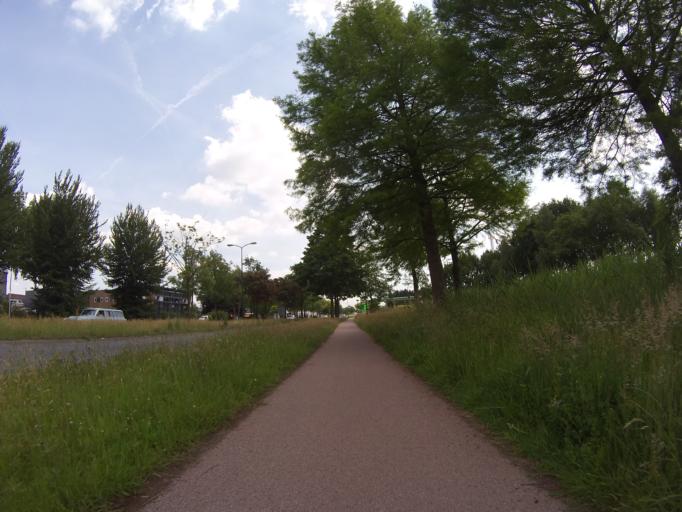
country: NL
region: Utrecht
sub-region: Gemeente Soest
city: Soest
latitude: 52.1788
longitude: 5.2698
